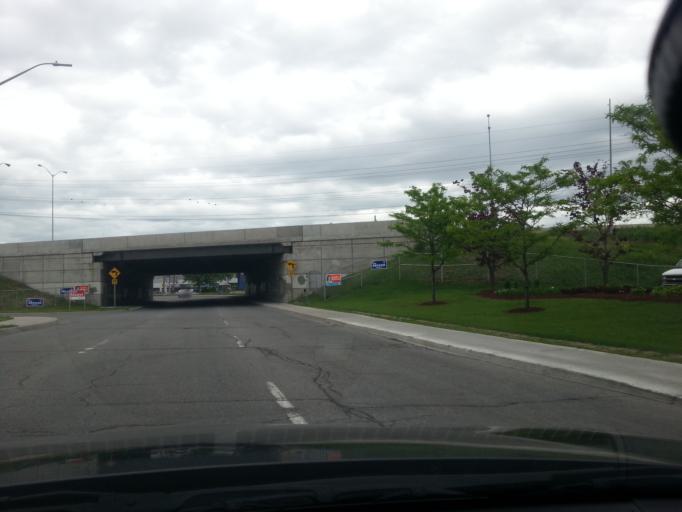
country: CA
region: Ontario
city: Ottawa
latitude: 45.3815
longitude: -75.7438
